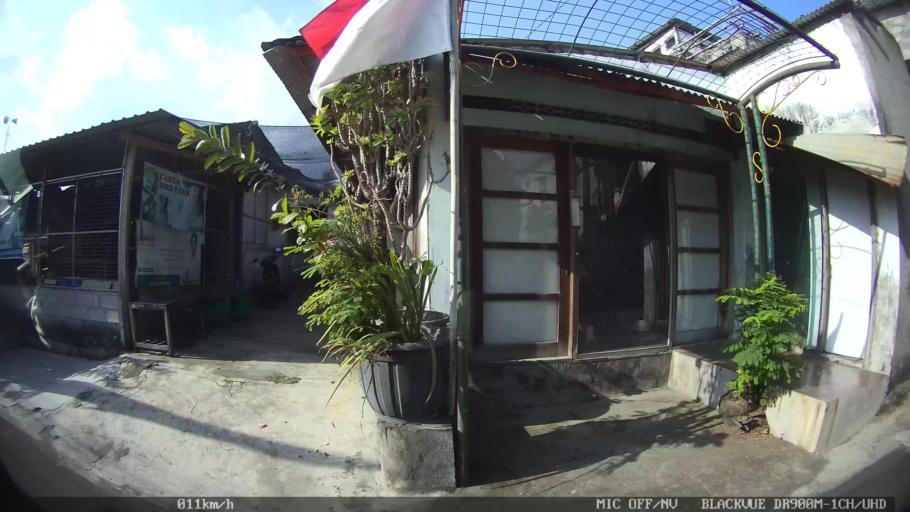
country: ID
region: Daerah Istimewa Yogyakarta
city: Yogyakarta
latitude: -7.7984
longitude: 110.3497
